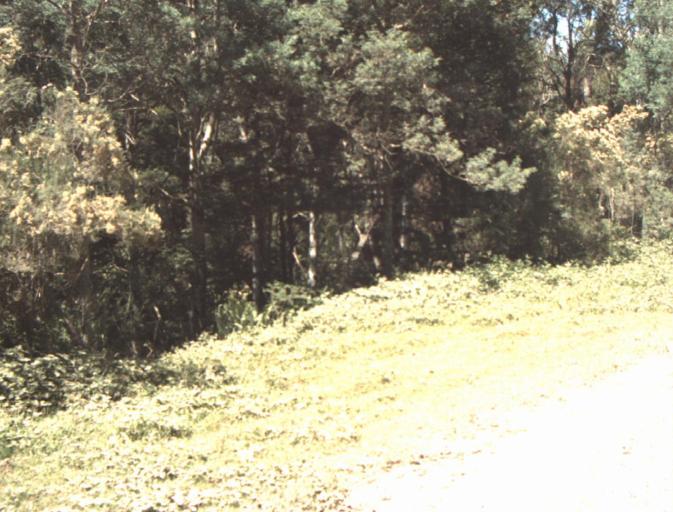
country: AU
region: Tasmania
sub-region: Dorset
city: Scottsdale
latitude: -41.3198
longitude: 147.4146
